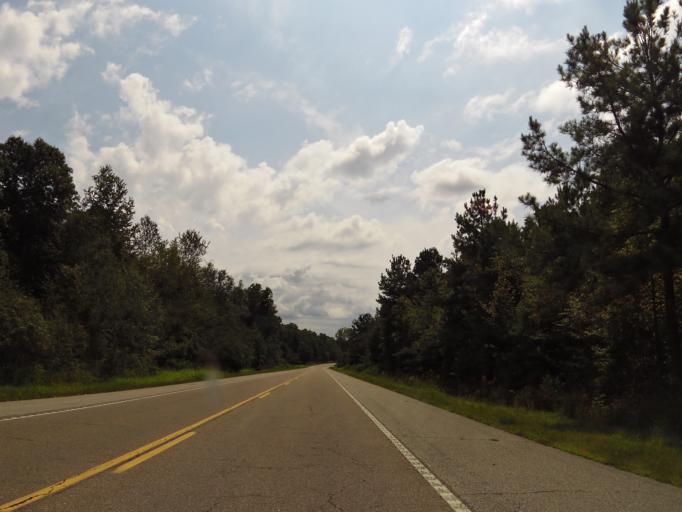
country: US
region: Tennessee
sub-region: Decatur County
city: Parsons
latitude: 35.6259
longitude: -88.0483
